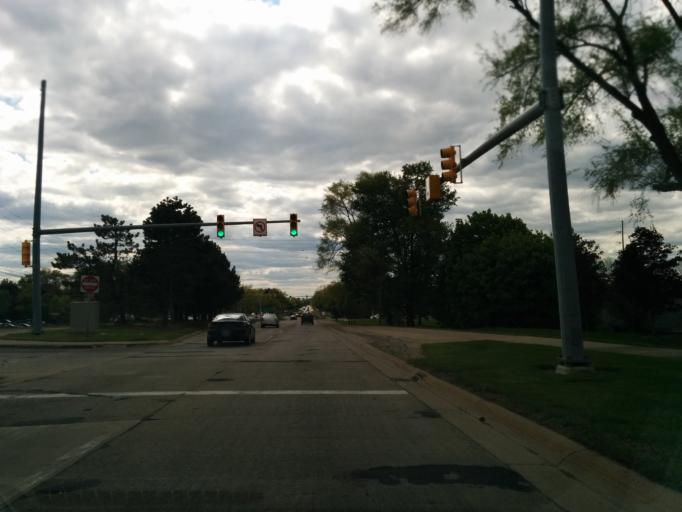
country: US
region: Michigan
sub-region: Oakland County
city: Farmington Hills
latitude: 42.4982
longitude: -83.3957
